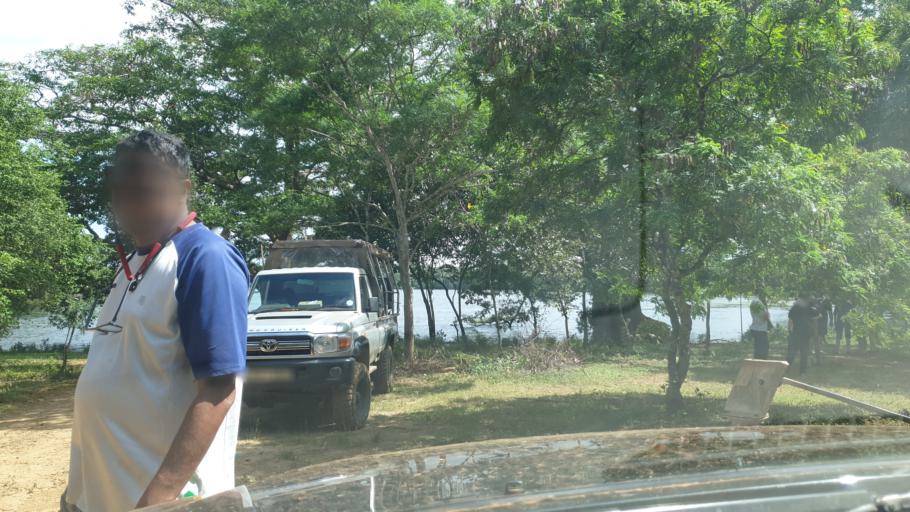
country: LK
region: North Central
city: Anuradhapura
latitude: 8.4218
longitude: 80.0045
